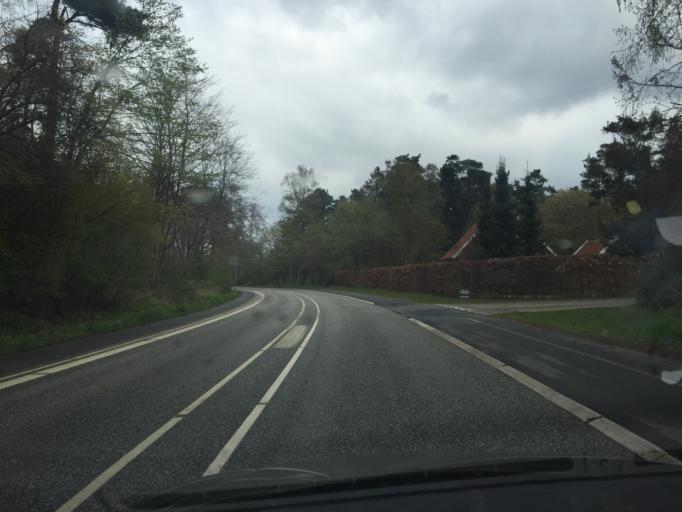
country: DK
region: Capital Region
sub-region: Halsnaes Kommune
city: Frederiksvaerk
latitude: 55.9983
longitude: 12.0148
